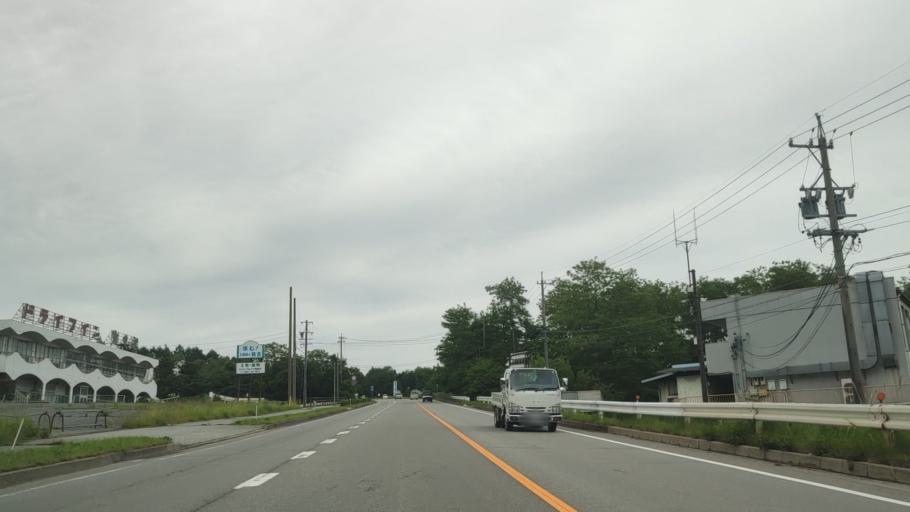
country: JP
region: Nagano
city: Komoro
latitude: 36.3335
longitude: 138.5260
